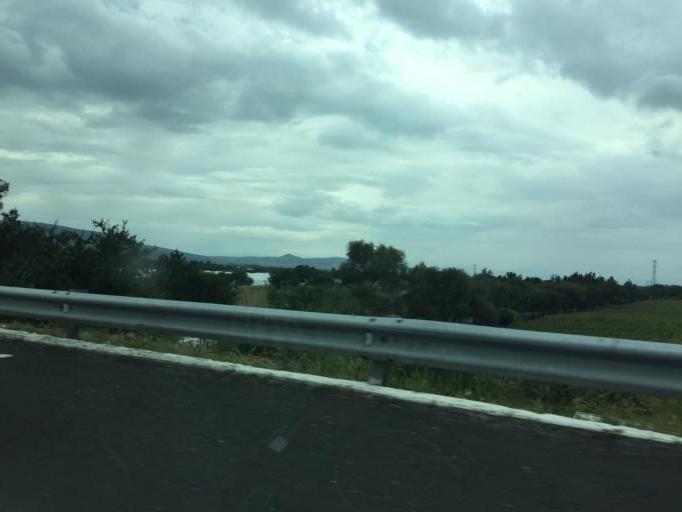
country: MX
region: Jalisco
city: Ocotlan
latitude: 20.3996
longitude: -102.7326
